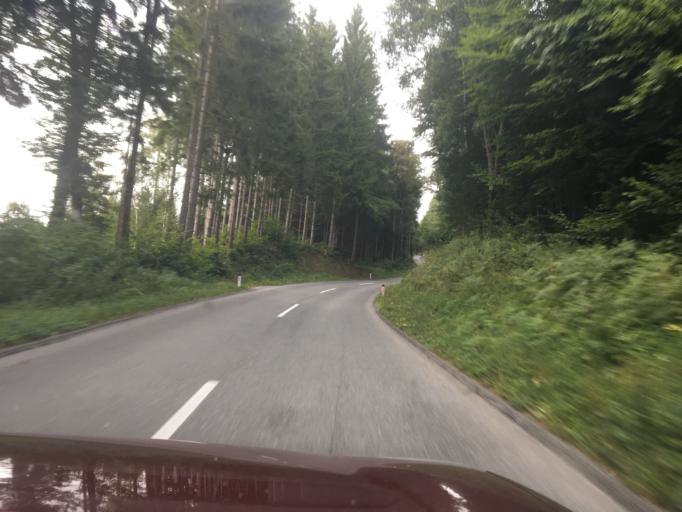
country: AT
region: Styria
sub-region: Politischer Bezirk Deutschlandsberg
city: Trahutten
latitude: 46.8084
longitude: 15.1704
